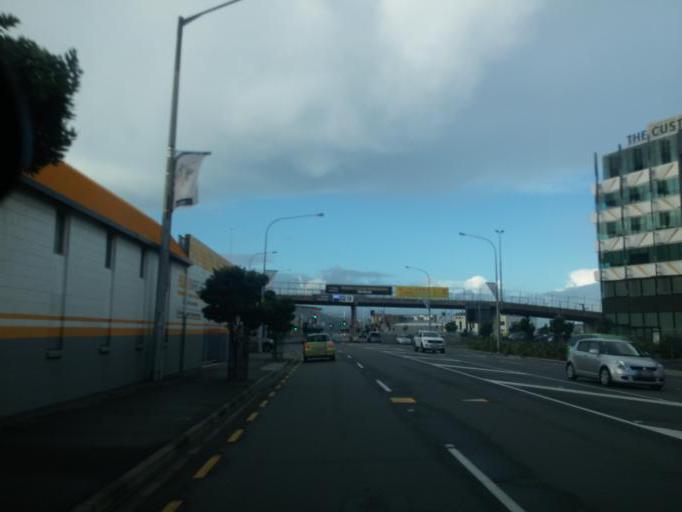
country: NZ
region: Wellington
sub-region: Wellington City
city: Wellington
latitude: -41.2776
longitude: 174.7827
